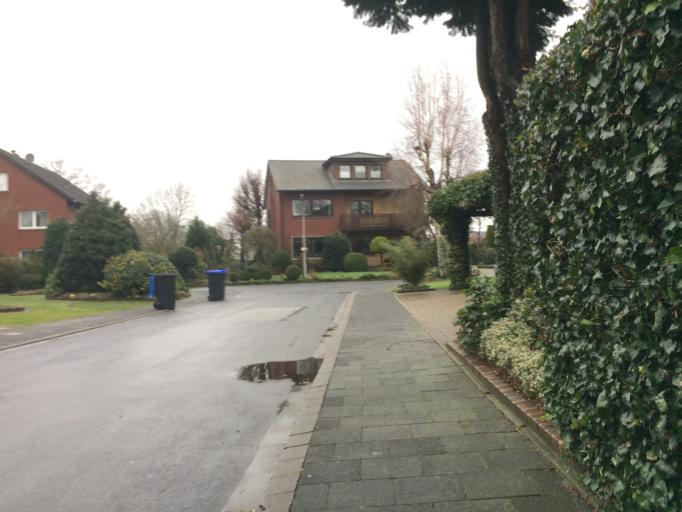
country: DE
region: North Rhine-Westphalia
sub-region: Regierungsbezirk Munster
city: Beelen
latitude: 51.9329
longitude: 8.1131
